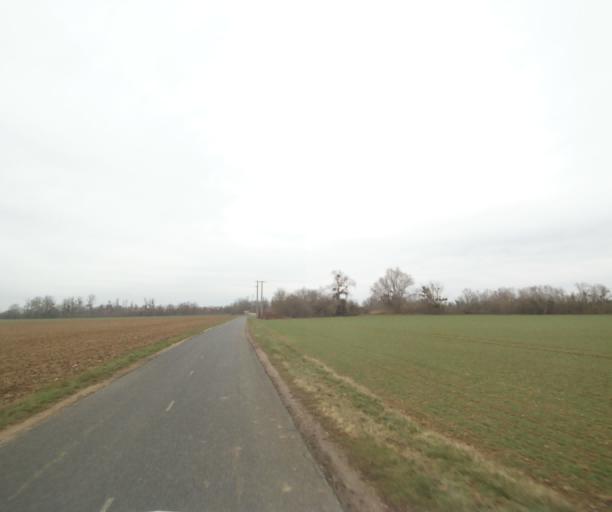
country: FR
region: Champagne-Ardenne
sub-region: Departement de la Haute-Marne
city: Villiers-en-Lieu
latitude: 48.6482
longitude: 4.8316
